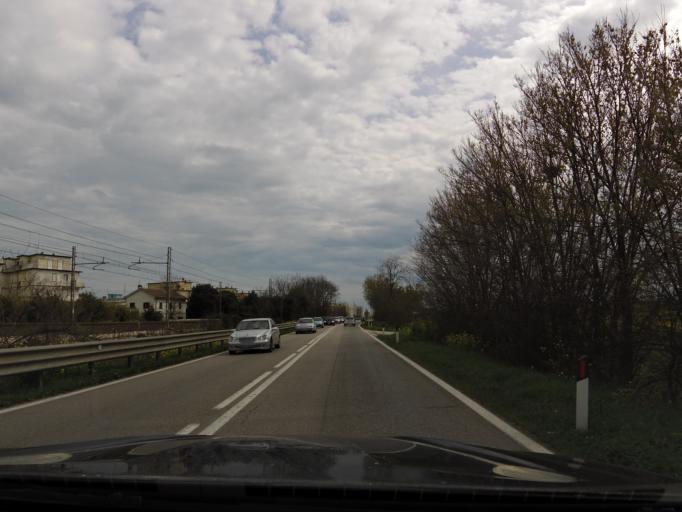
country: IT
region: The Marches
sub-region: Provincia di Macerata
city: Porto Recanati
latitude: 43.4135
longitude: 13.6727
